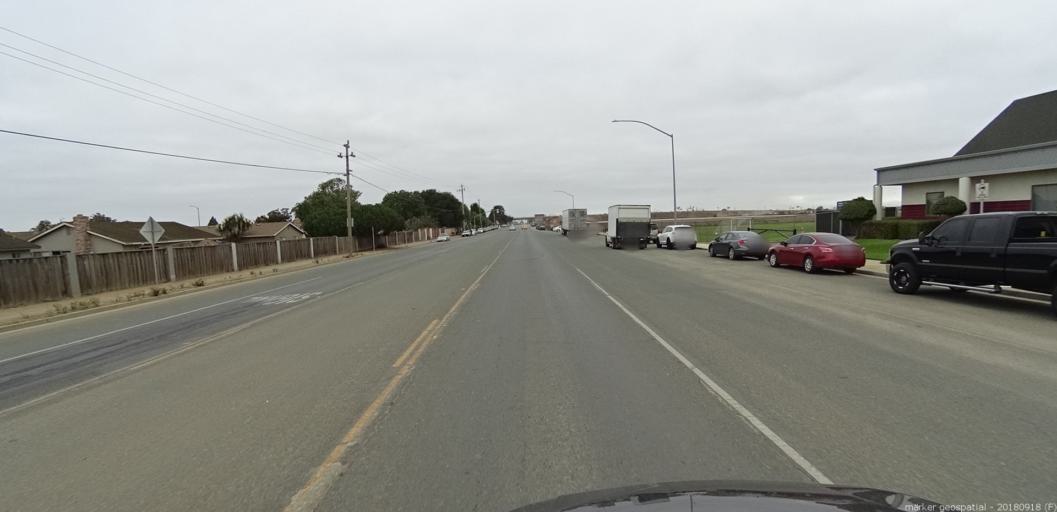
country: US
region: California
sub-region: Monterey County
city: Boronda
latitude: 36.7326
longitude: -121.6494
